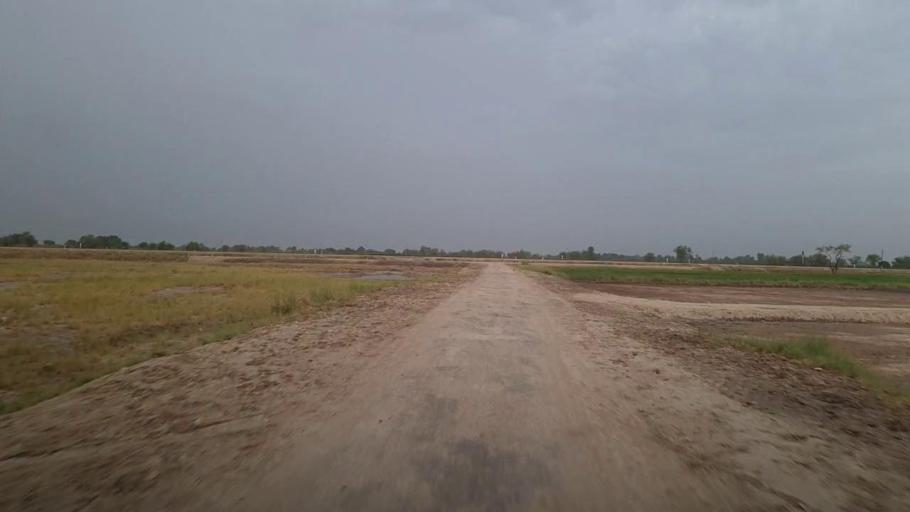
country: PK
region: Sindh
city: Karaundi
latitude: 26.9998
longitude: 68.3491
